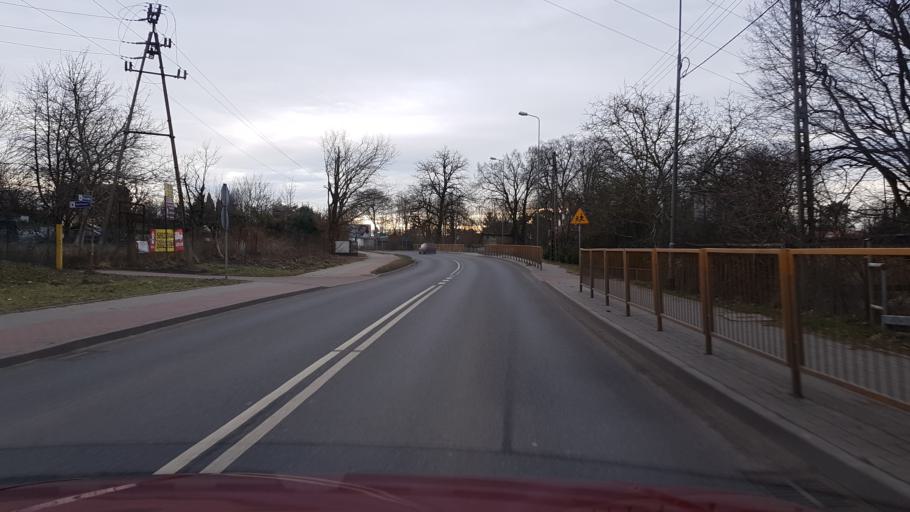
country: PL
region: West Pomeranian Voivodeship
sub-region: Powiat policki
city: Dobra
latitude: 53.4965
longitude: 14.4810
